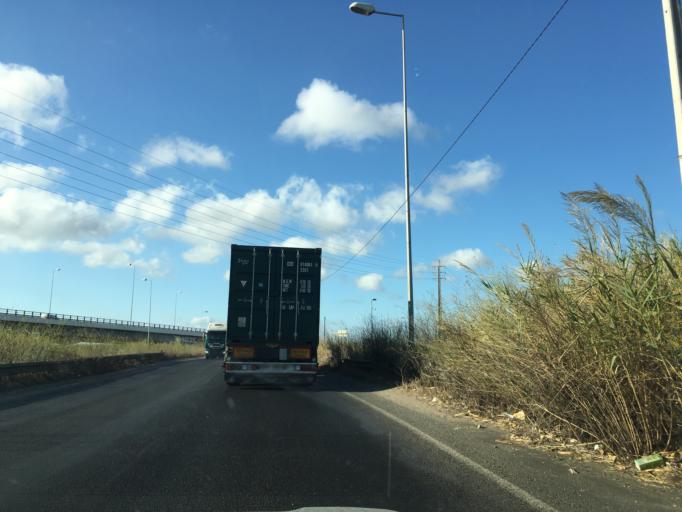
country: PT
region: Lisbon
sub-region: Loures
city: Santa Iria da Azoia
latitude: 38.8349
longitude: -9.0778
